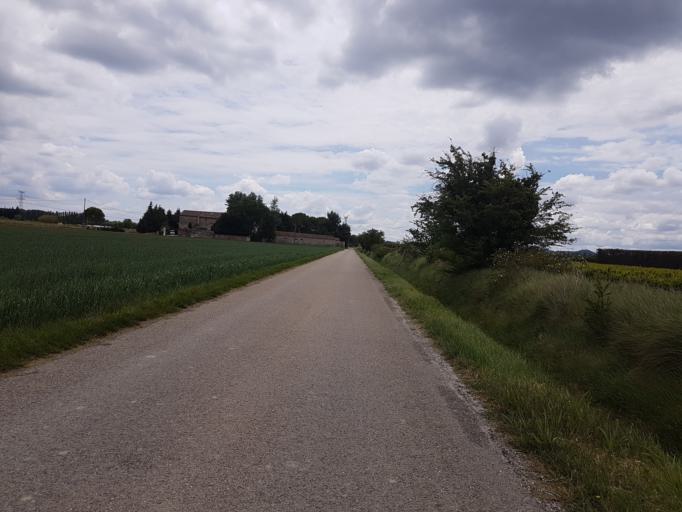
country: FR
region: Languedoc-Roussillon
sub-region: Departement du Gard
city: Vallabregues
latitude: 43.8872
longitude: 4.6335
